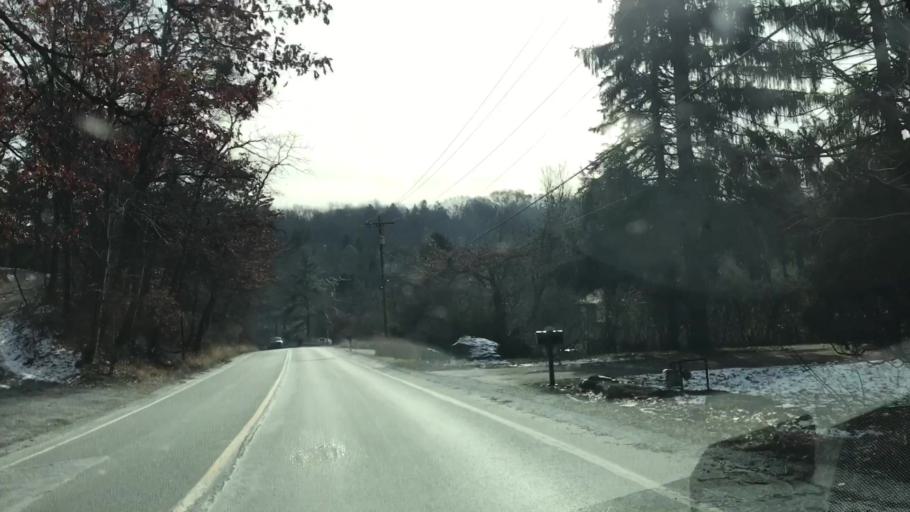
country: US
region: Pennsylvania
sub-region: Allegheny County
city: Franklin Park
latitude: 40.5945
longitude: -80.0775
